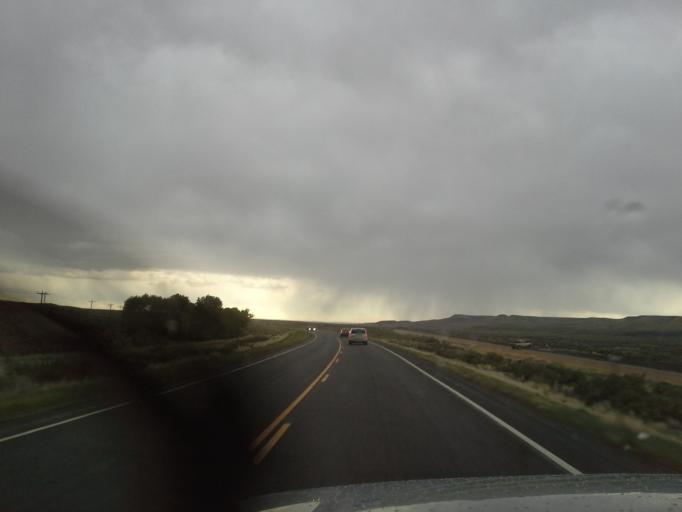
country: US
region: Wyoming
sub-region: Park County
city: Powell
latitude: 45.0485
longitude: -108.6533
